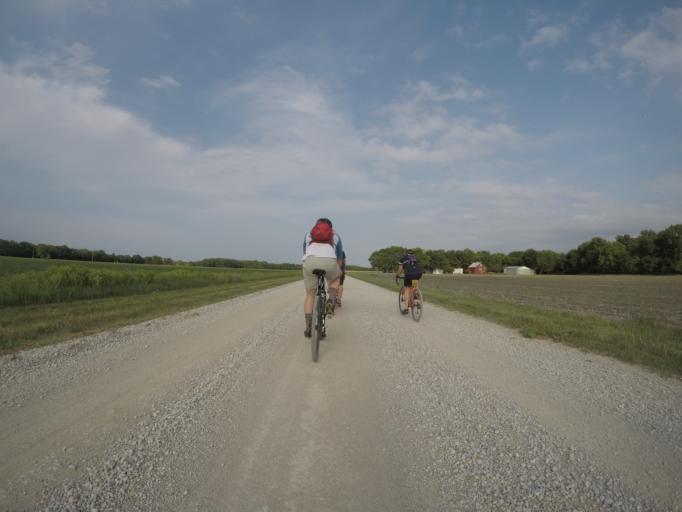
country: US
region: Kansas
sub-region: Riley County
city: Manhattan
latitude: 39.1230
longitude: -96.4659
